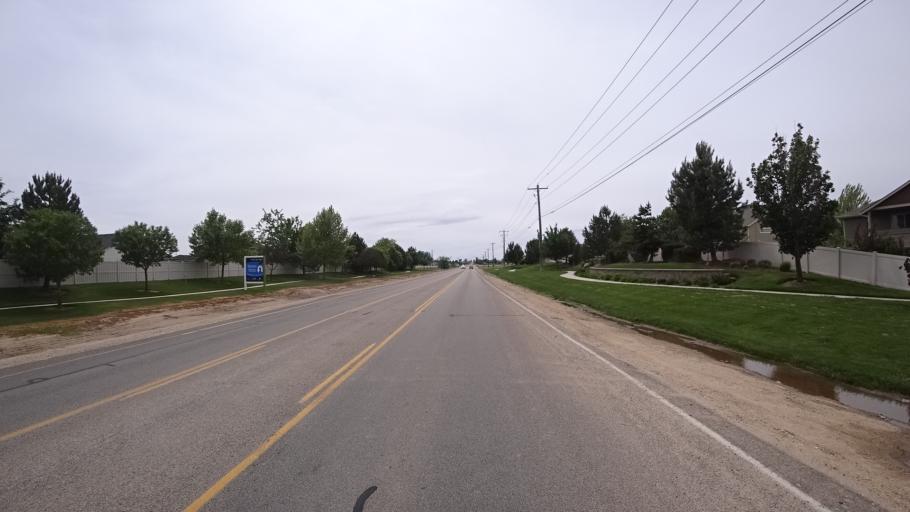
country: US
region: Idaho
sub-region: Ada County
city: Meridian
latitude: 43.5663
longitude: -116.3545
